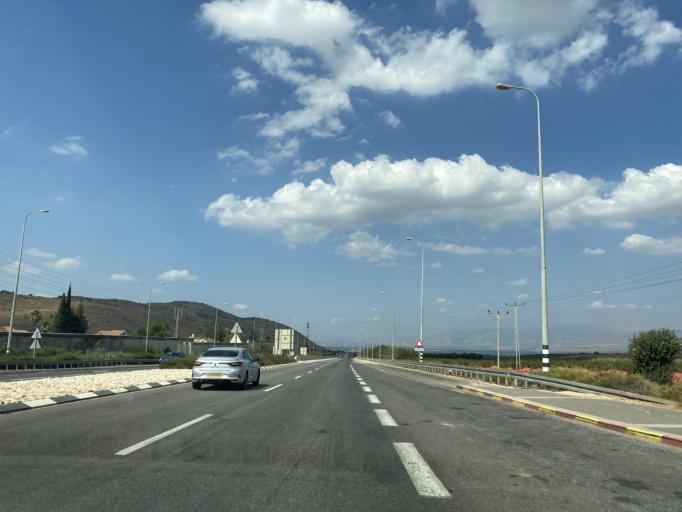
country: IL
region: Northern District
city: Rosh Pinna
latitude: 33.0466
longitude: 35.5721
